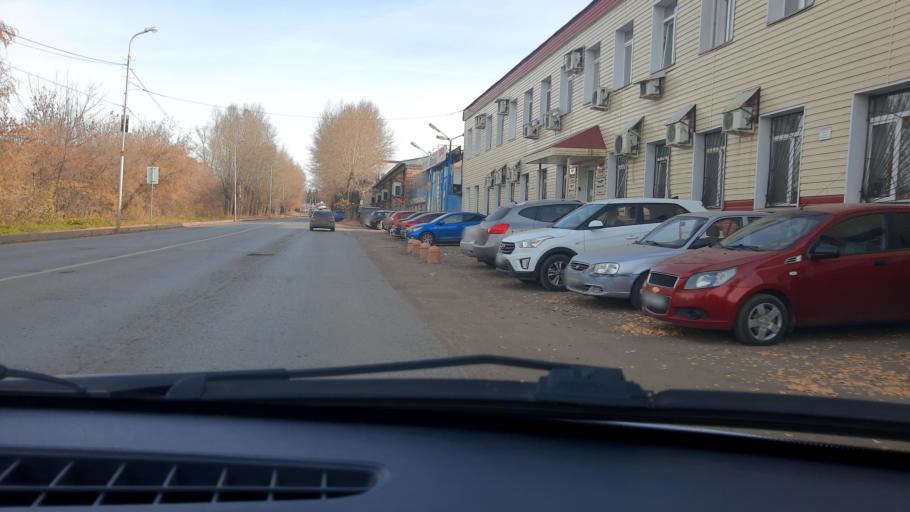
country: RU
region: Bashkortostan
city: Ufa
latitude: 54.8056
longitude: 56.0759
